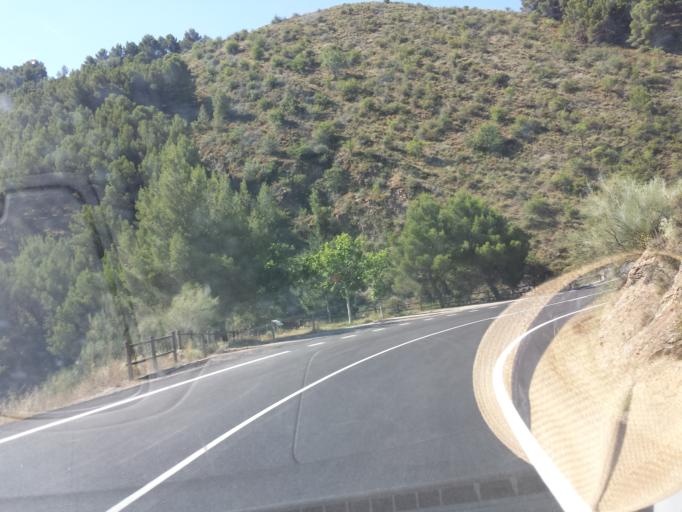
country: ES
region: Aragon
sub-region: Provincia de Zaragoza
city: Nuevalos
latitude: 41.2145
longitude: -1.7564
